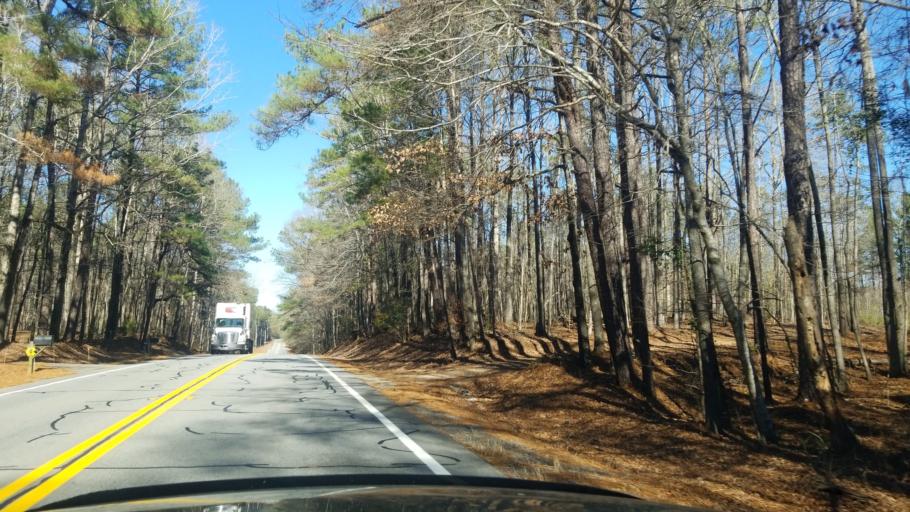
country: US
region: Georgia
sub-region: Harris County
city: Hamilton
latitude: 32.6685
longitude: -84.8588
